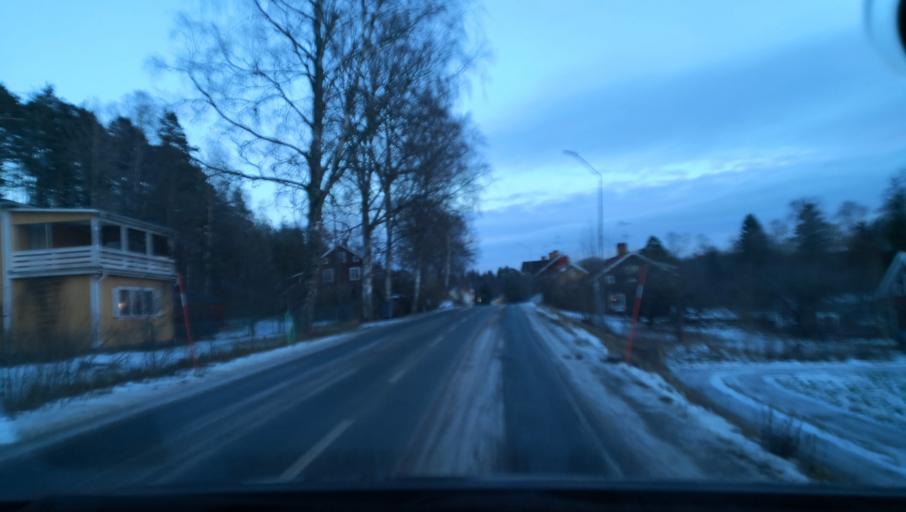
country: SE
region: Soedermanland
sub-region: Katrineholms Kommun
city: Katrineholm
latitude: 59.0898
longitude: 16.2102
